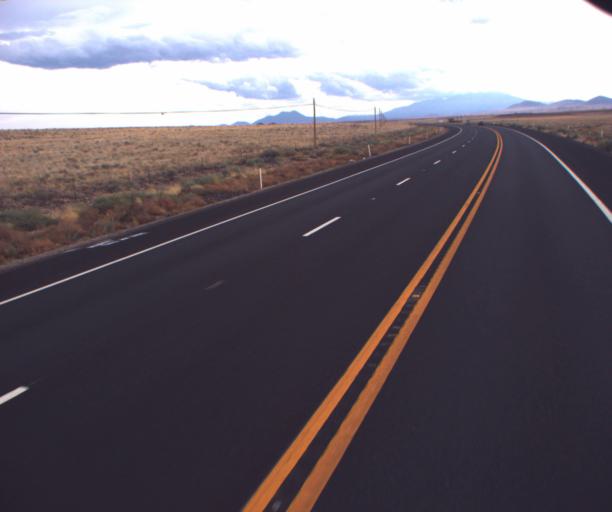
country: US
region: Arizona
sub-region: Coconino County
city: Tuba City
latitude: 35.6926
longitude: -111.5034
